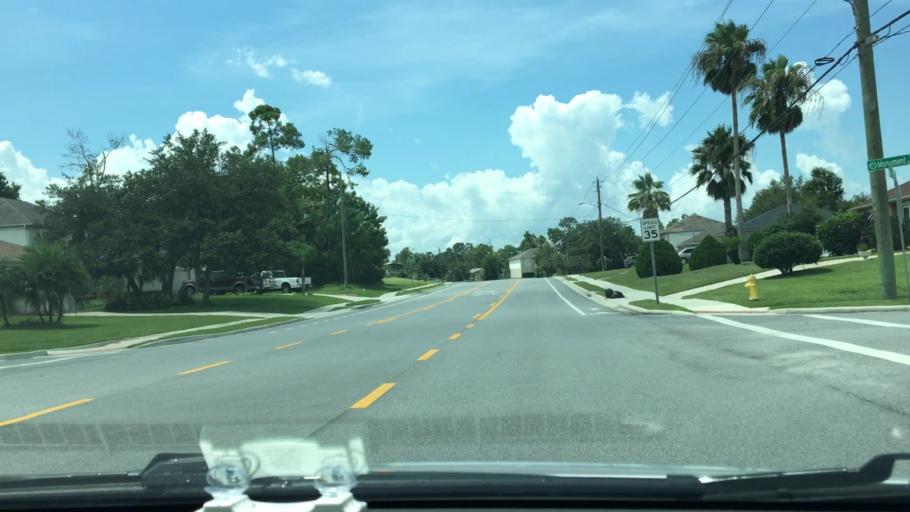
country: US
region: Florida
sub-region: Volusia County
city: Deltona
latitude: 28.8790
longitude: -81.1612
